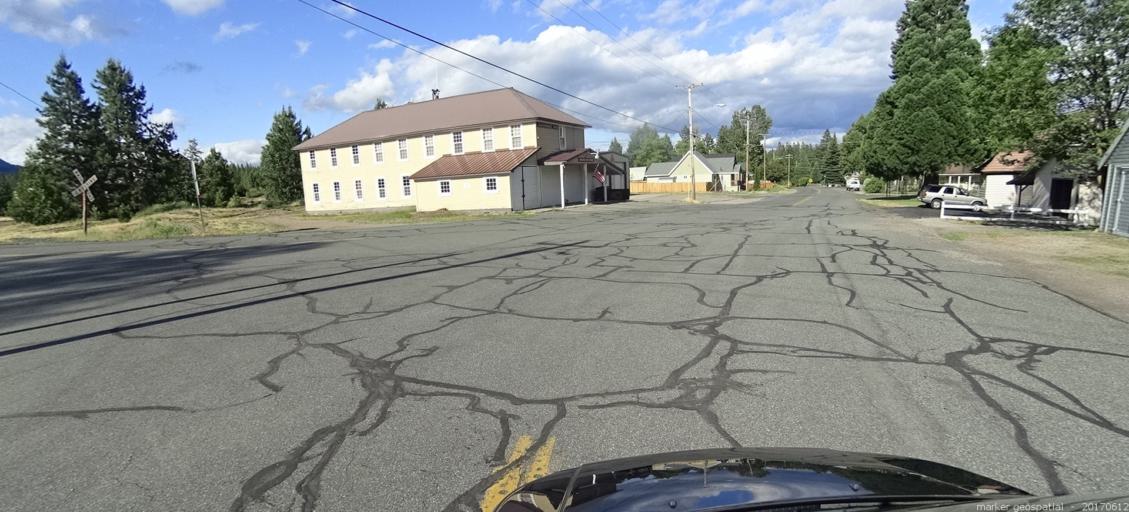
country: US
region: California
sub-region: Siskiyou County
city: McCloud
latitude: 41.2583
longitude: -122.1389
